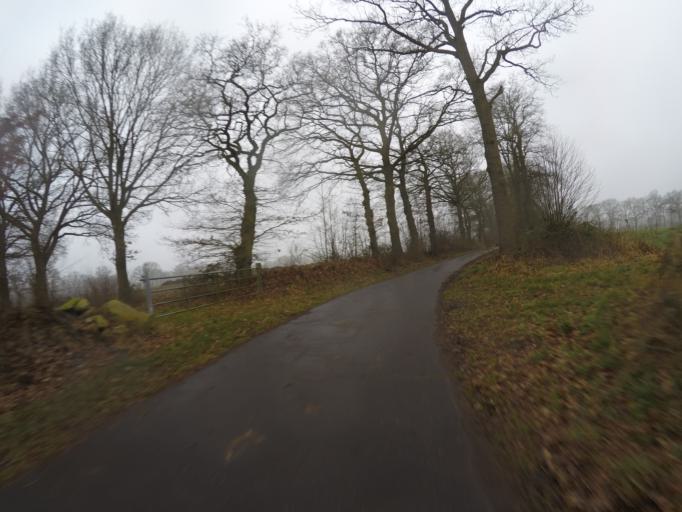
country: DE
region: Schleswig-Holstein
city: Quickborn
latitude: 53.7051
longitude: 9.9295
